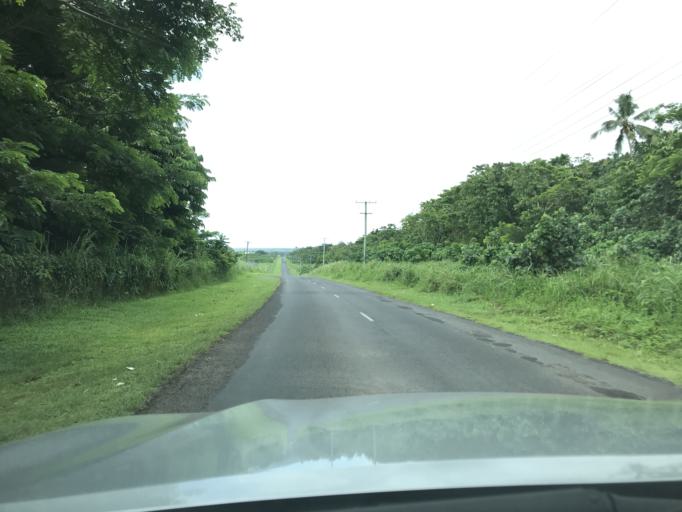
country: WS
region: Aiga-i-le-Tai
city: Mulifanua
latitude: -13.8340
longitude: -172.0160
